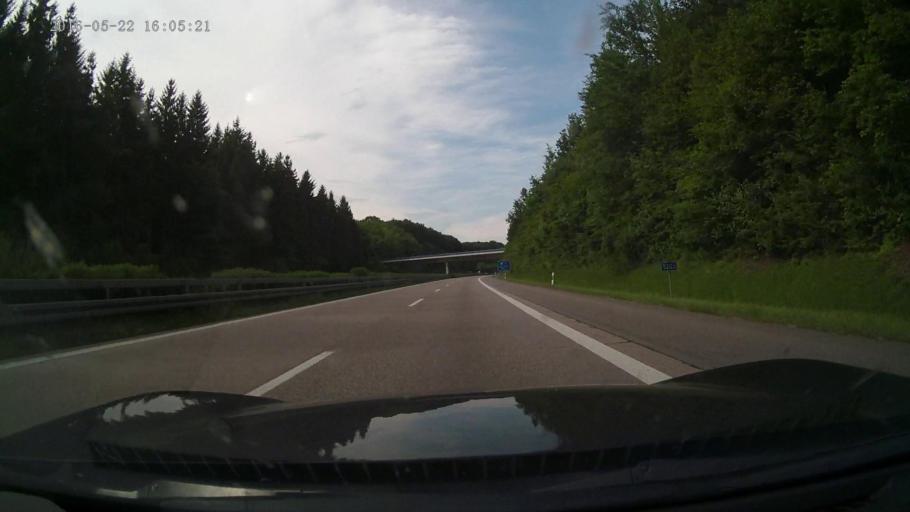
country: DE
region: Baden-Wuerttemberg
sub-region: Regierungsbezirk Stuttgart
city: Neuenstadt am Kocher
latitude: 49.2679
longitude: 9.3522
